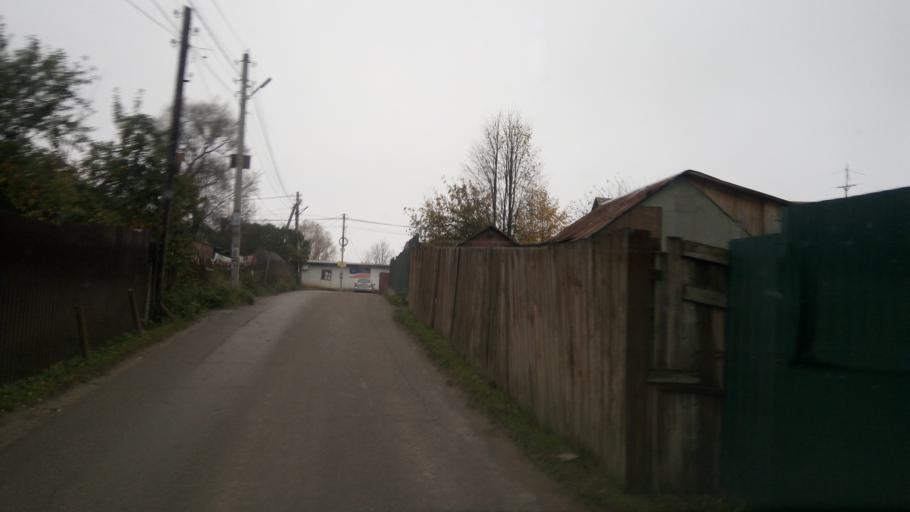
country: RU
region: Moskovskaya
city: Skhodnya
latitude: 55.9340
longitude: 37.2873
